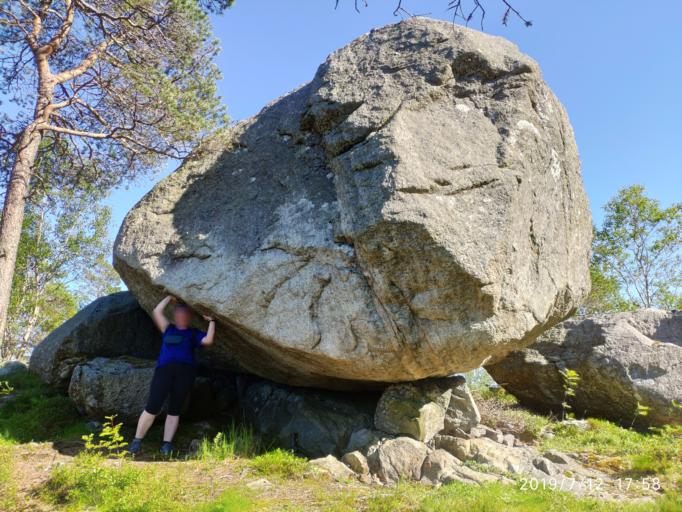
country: NO
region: Rogaland
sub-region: Forsand
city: Forsand
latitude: 59.0009
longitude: 6.1748
